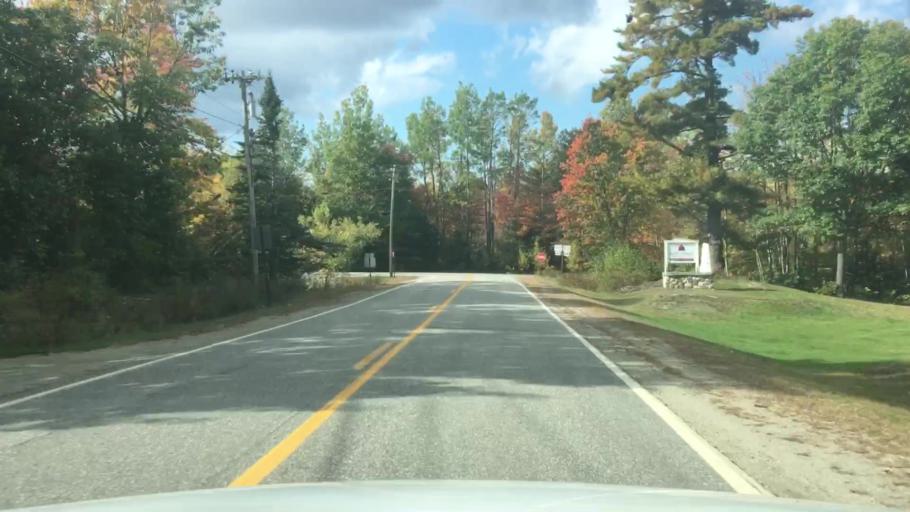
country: US
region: Maine
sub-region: Knox County
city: Washington
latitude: 44.3203
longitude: -69.3602
